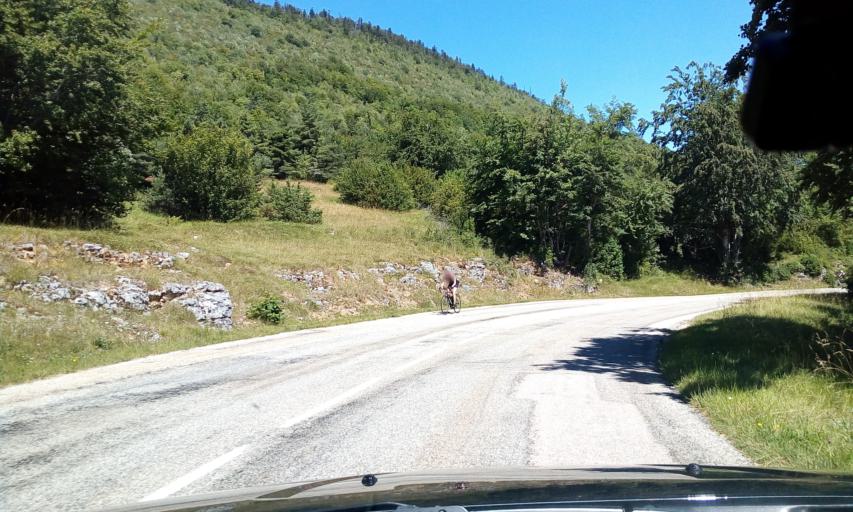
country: FR
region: Rhone-Alpes
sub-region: Departement de la Drome
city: Saint-Laurent-en-Royans
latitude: 44.9363
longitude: 5.3832
